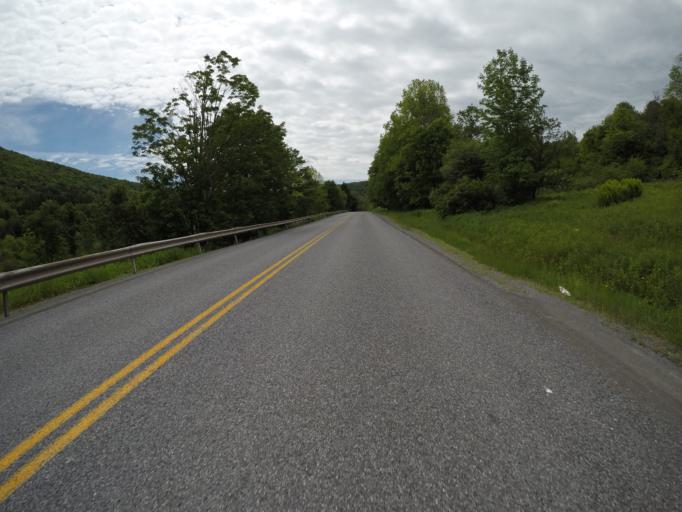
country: US
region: New York
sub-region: Delaware County
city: Stamford
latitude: 42.1898
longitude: -74.5829
